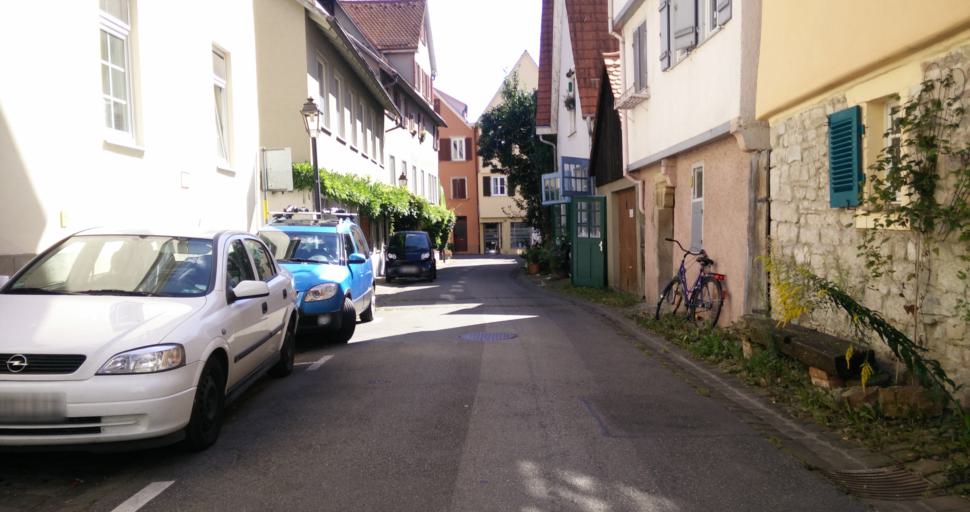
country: DE
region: Baden-Wuerttemberg
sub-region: Tuebingen Region
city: Tuebingen
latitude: 48.5224
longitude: 9.0513
